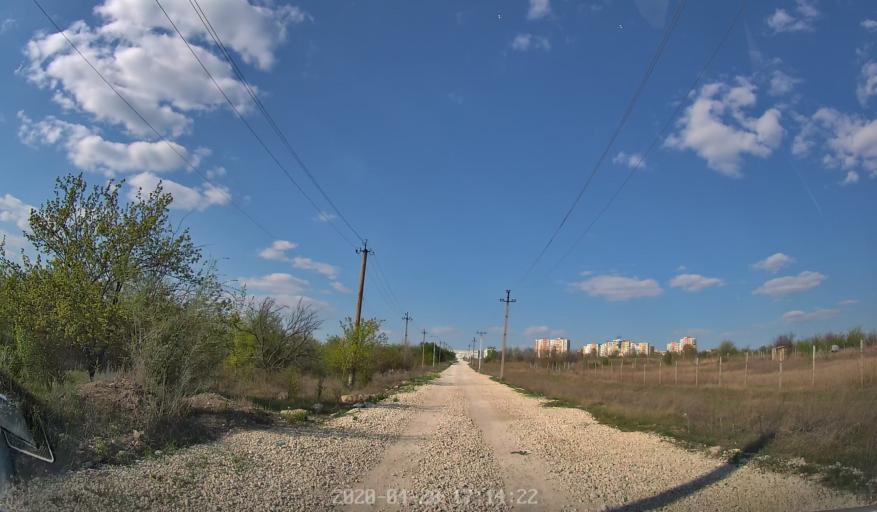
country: MD
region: Chisinau
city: Chisinau
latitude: 46.9678
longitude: 28.8434
